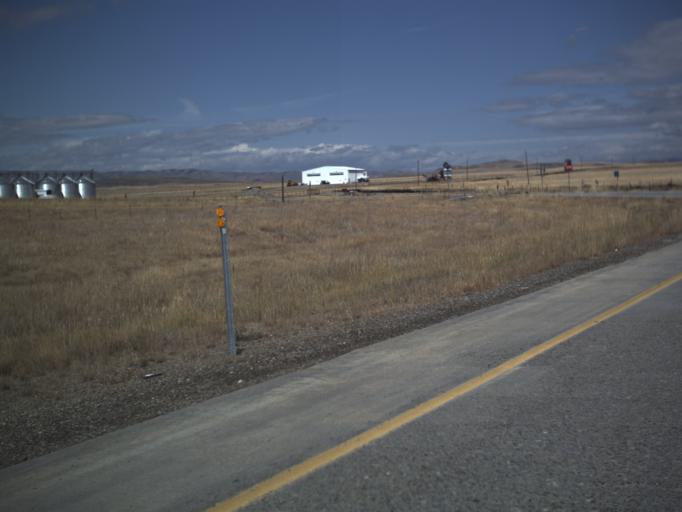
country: US
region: Utah
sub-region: Box Elder County
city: Garland
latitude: 41.8406
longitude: -112.4351
